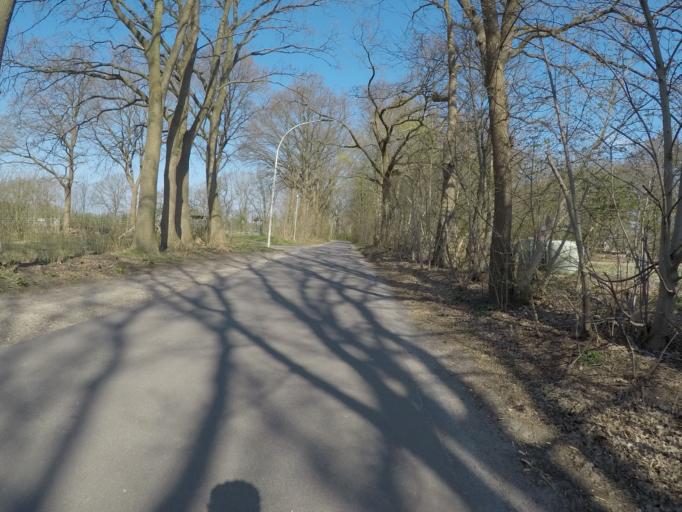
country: DE
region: Schleswig-Holstein
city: Halstenbek
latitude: 53.5976
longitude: 9.8120
